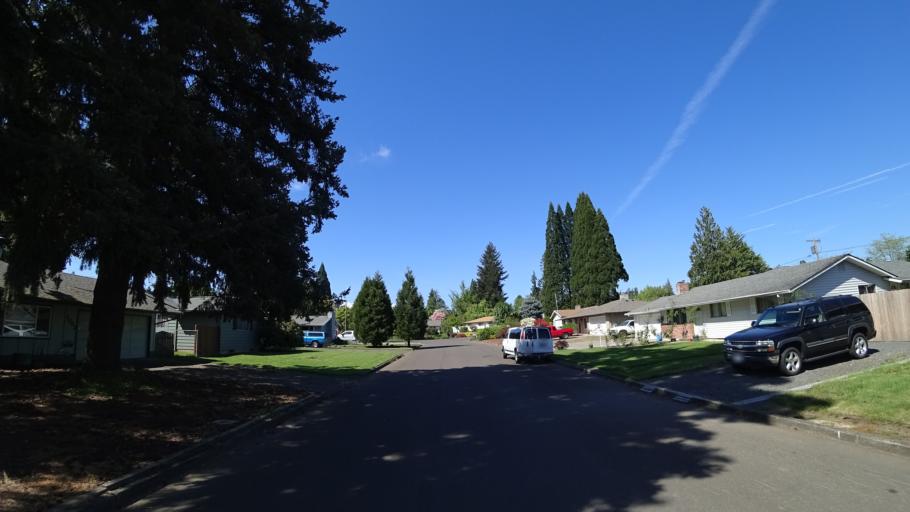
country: US
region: Oregon
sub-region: Washington County
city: Hillsboro
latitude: 45.5116
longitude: -122.9595
